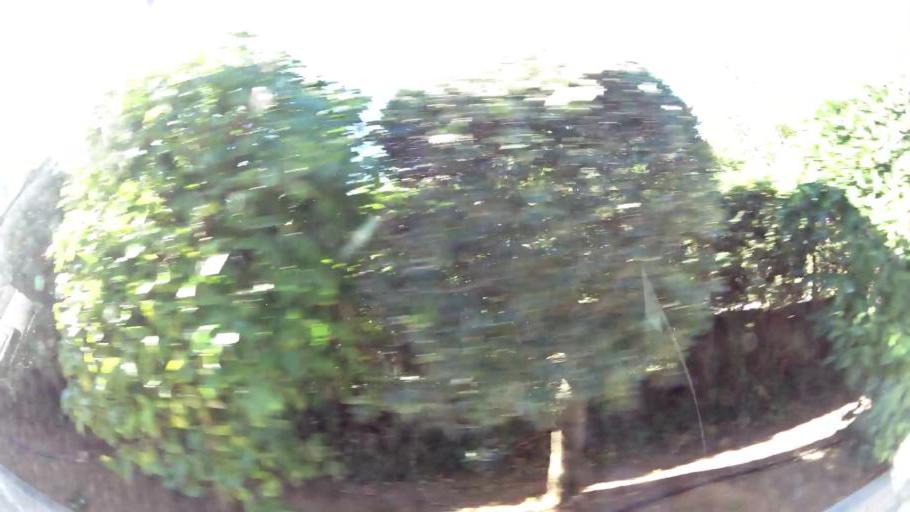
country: GR
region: Attica
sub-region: Nomarchia Athinas
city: Melissia
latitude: 38.0410
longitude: 23.8443
